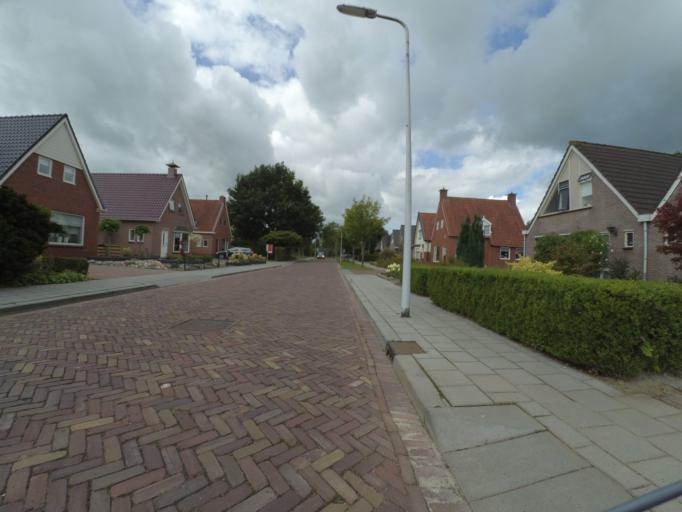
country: NL
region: Friesland
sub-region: Gemeente Achtkarspelen
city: Buitenpost
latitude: 53.2558
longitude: 6.1474
